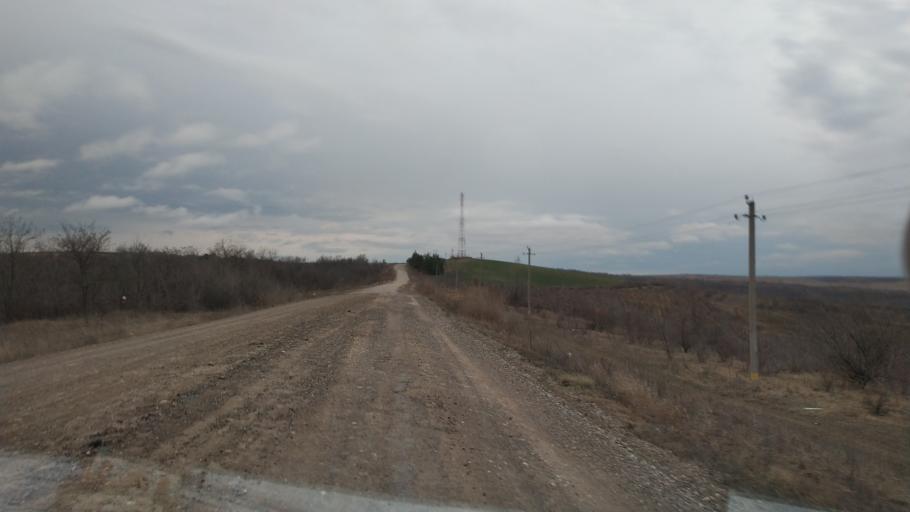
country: MD
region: Causeni
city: Causeni
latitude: 46.6214
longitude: 29.3945
